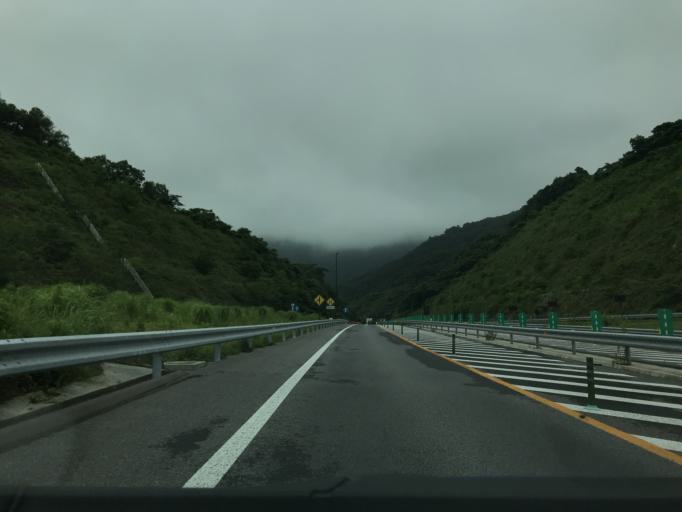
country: JP
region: Oita
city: Bungo-Takada-shi
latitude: 33.4971
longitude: 131.3179
